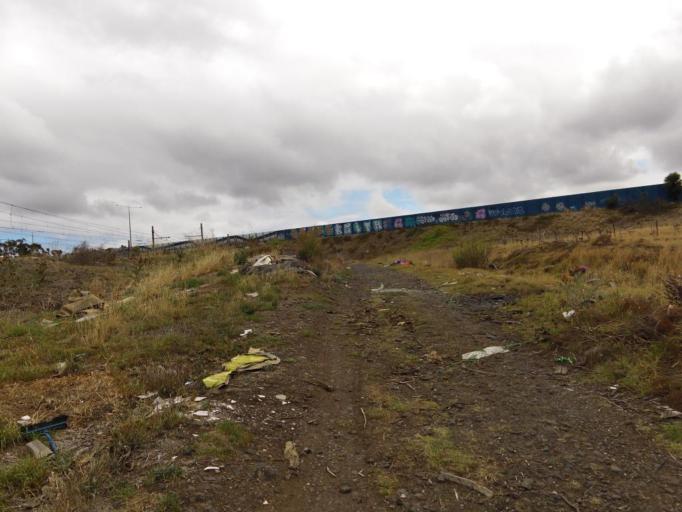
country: AU
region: Victoria
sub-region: Hobsons Bay
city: Laverton
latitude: -37.8619
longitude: 144.7784
